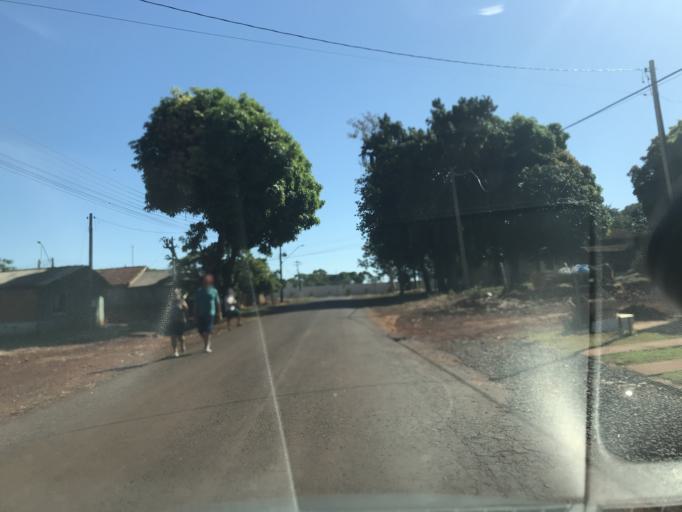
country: BR
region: Parana
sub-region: Palotina
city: Palotina
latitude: -24.2659
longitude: -53.8343
